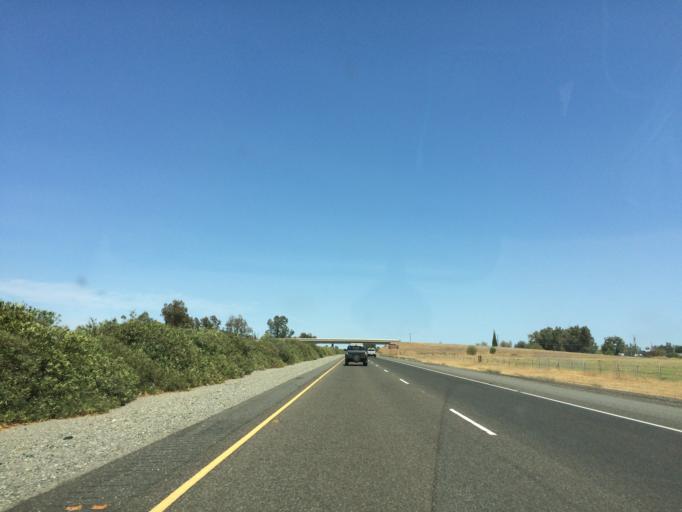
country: US
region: California
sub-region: Glenn County
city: Orland
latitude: 39.7228
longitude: -122.2059
